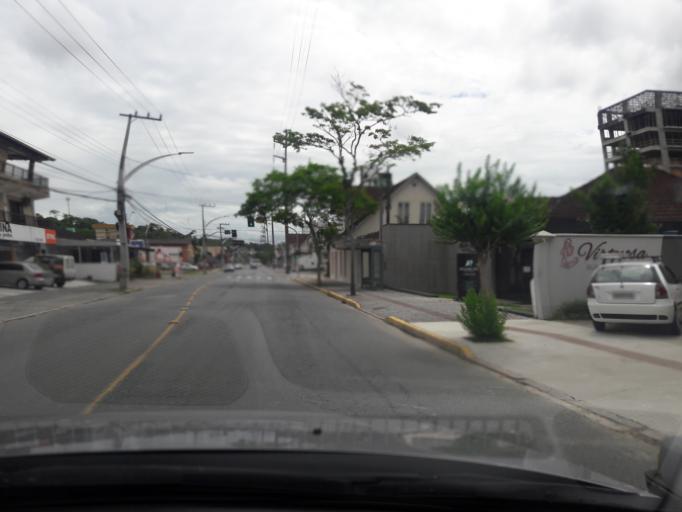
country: BR
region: Santa Catarina
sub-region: Joinville
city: Joinville
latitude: -26.3200
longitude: -48.8514
